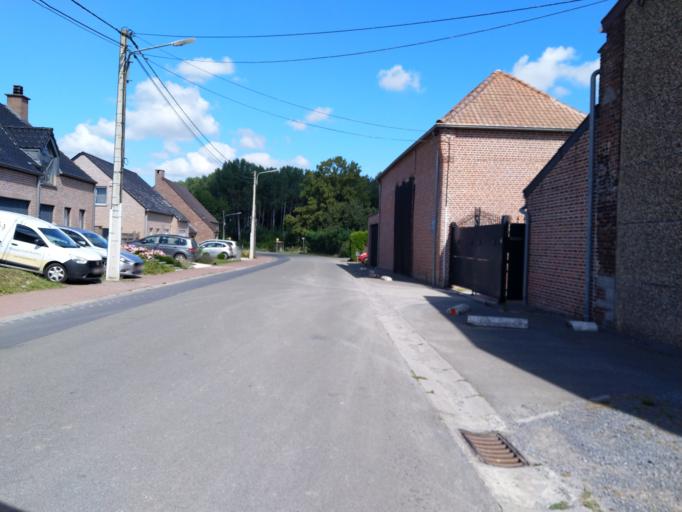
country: BE
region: Wallonia
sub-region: Province du Hainaut
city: Beloeil
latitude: 50.6001
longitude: 3.7125
